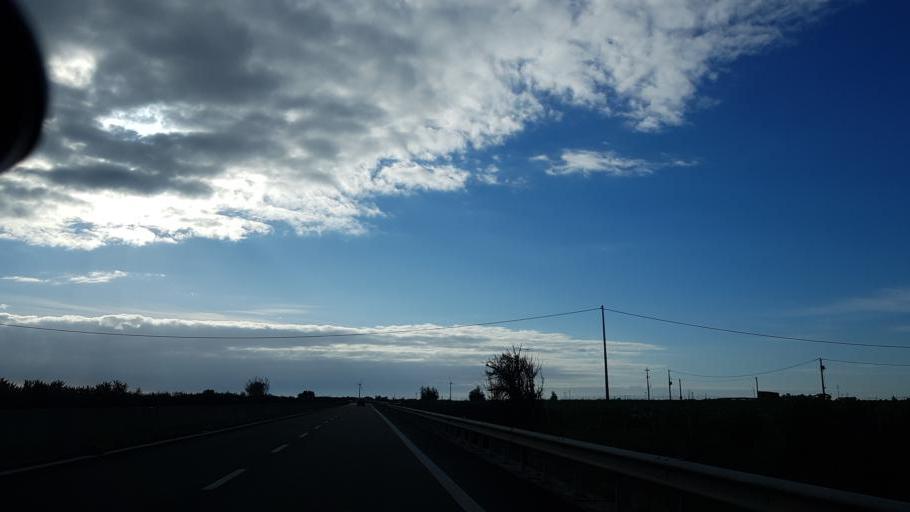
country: IT
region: Apulia
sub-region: Provincia di Brindisi
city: La Rosa
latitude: 40.5881
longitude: 17.9738
